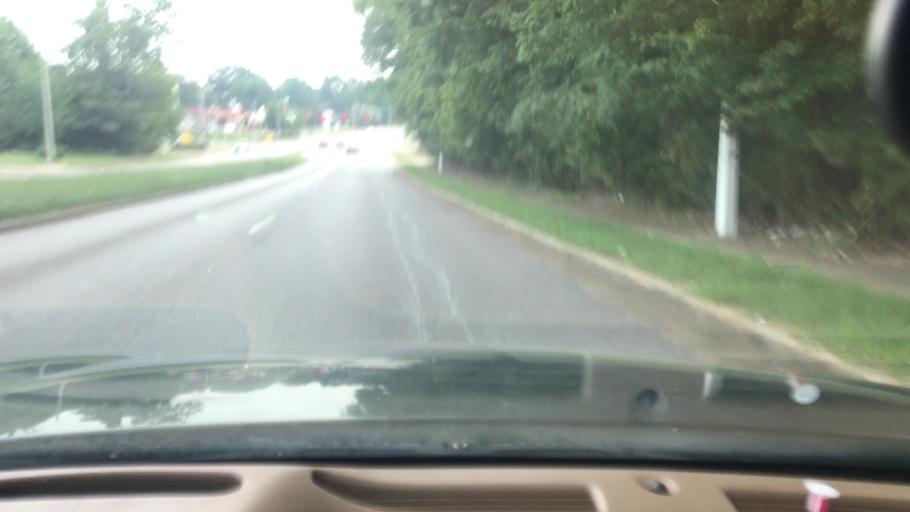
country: US
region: Tennessee
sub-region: Shelby County
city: Bartlett
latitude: 35.1812
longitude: -89.8714
